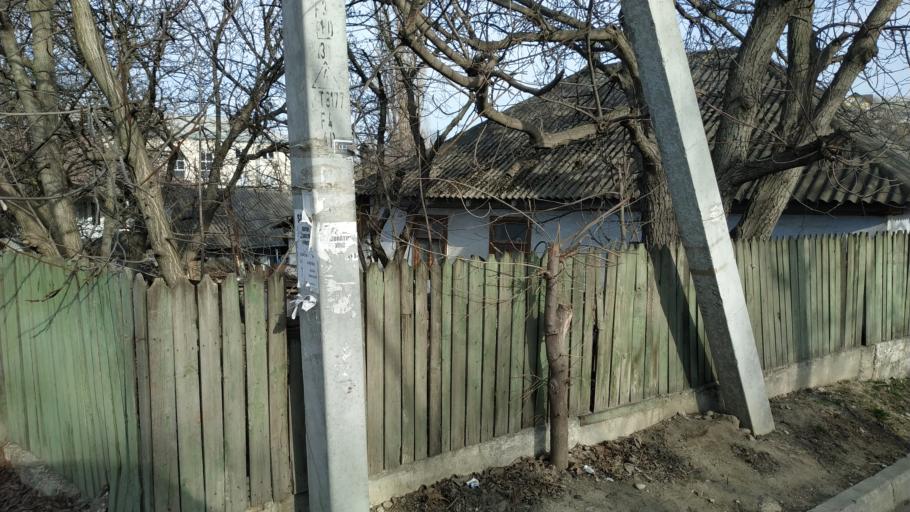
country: MD
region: Chisinau
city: Vatra
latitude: 47.0708
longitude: 28.6835
